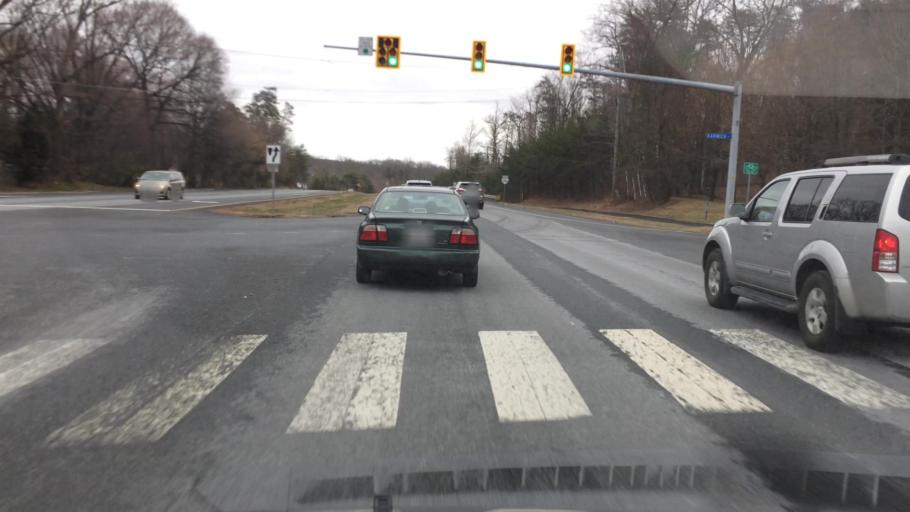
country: US
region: Virginia
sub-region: Fairfax County
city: Fairfax Station
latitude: 38.7801
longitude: -77.3045
